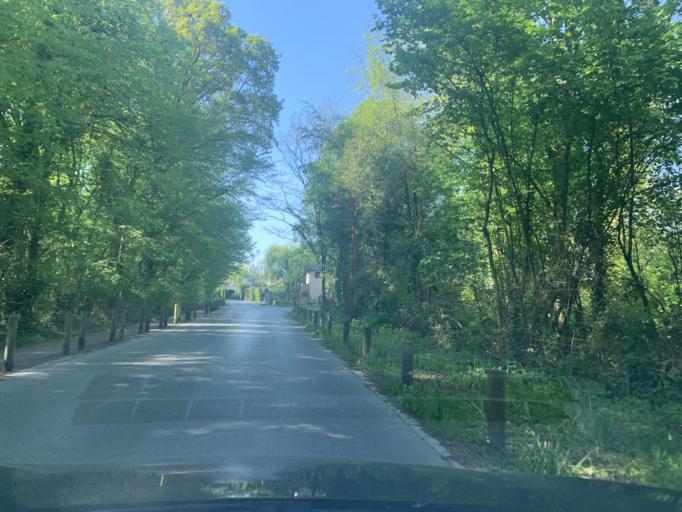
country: FR
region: Nord-Pas-de-Calais
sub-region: Departement du Nord
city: Proville
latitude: 50.1655
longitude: 3.2074
